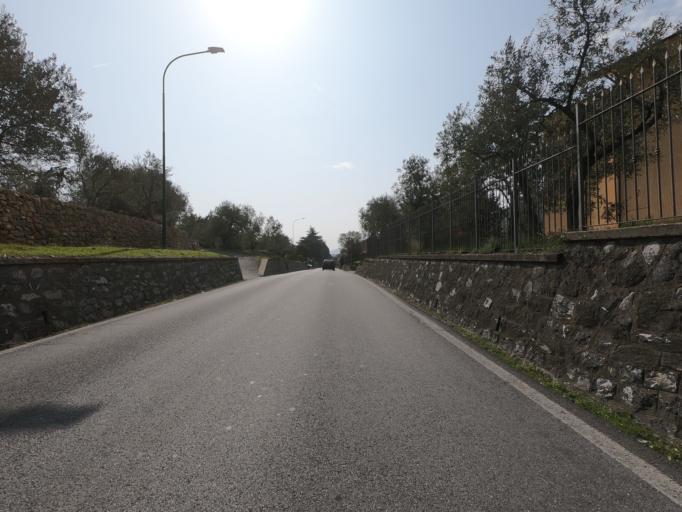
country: IT
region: Liguria
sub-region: Provincia di Savona
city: Cisano
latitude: 44.0872
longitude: 8.1471
